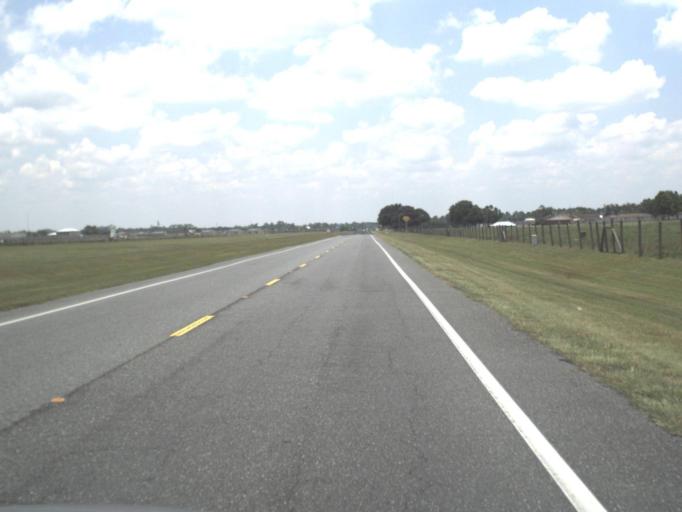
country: US
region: Florida
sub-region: Bradford County
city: Starke
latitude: 30.0548
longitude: -82.1758
